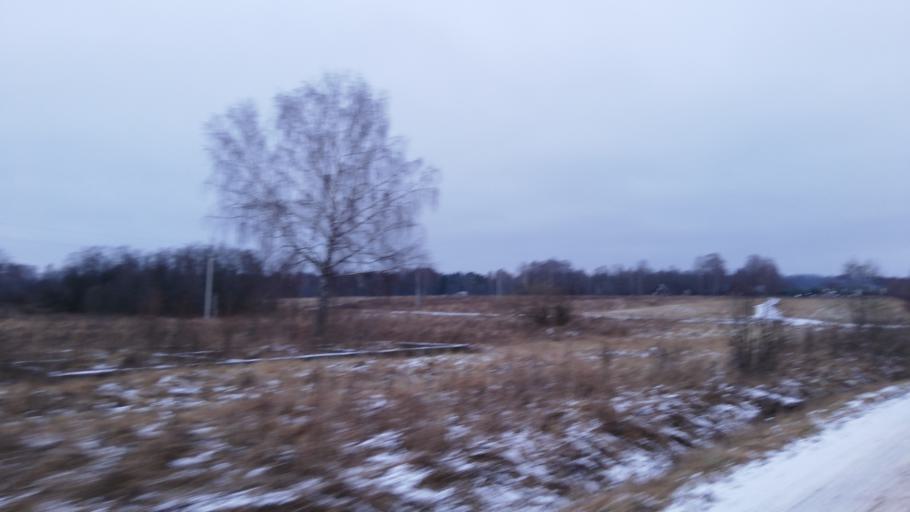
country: RU
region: Kostroma
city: Krasnoye-na-Volge
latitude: 57.6728
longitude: 41.1987
